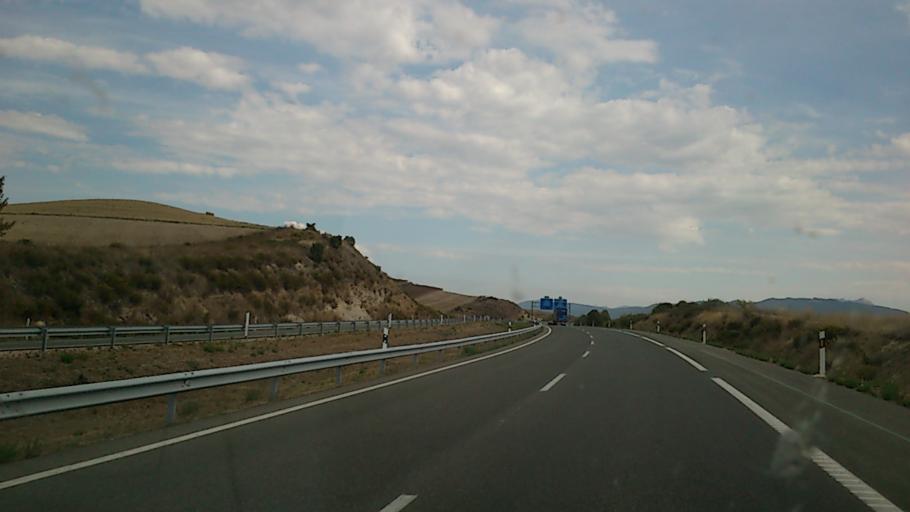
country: ES
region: Castille and Leon
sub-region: Provincia de Burgos
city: Miranda de Ebro
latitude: 42.7208
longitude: -2.9177
